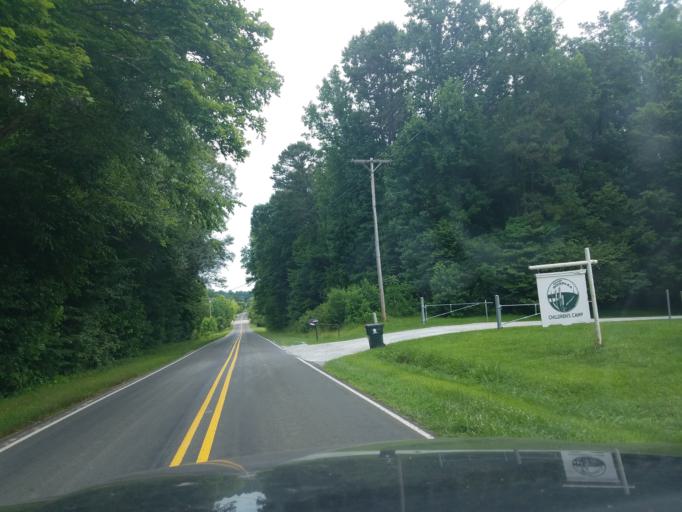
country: US
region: North Carolina
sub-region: Durham County
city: Durham
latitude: 36.1475
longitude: -78.9472
